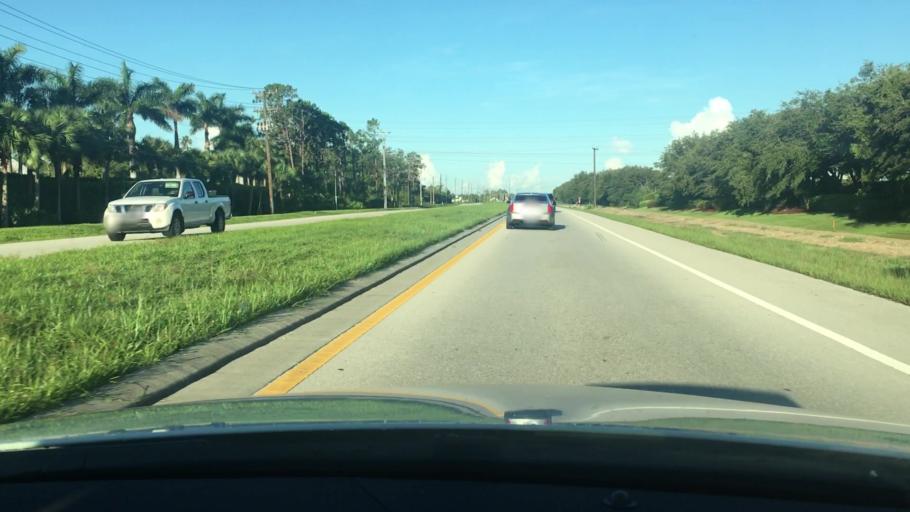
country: US
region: Florida
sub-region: Lee County
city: Three Oaks
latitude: 26.4444
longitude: -81.7533
